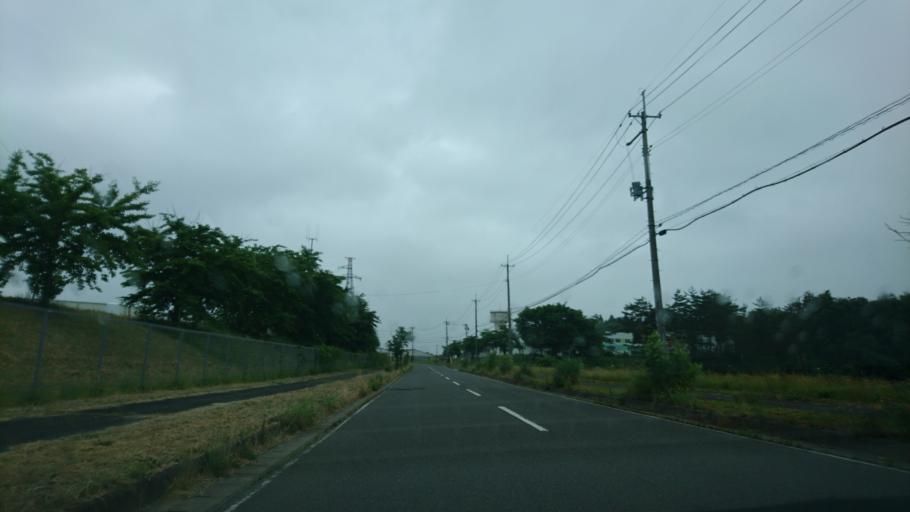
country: JP
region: Iwate
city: Ichinoseki
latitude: 38.9215
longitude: 141.1673
